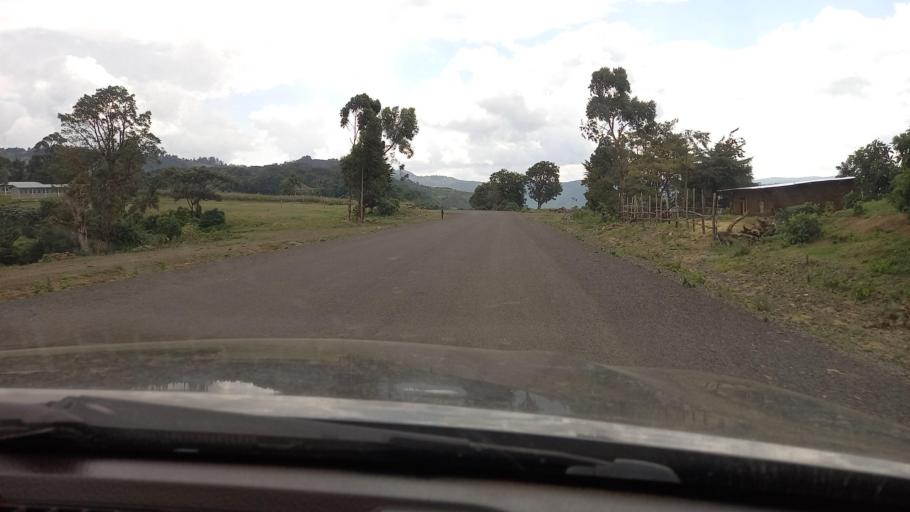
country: ET
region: Southern Nations, Nationalities, and People's Region
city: Mizan Teferi
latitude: 6.2143
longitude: 35.6162
